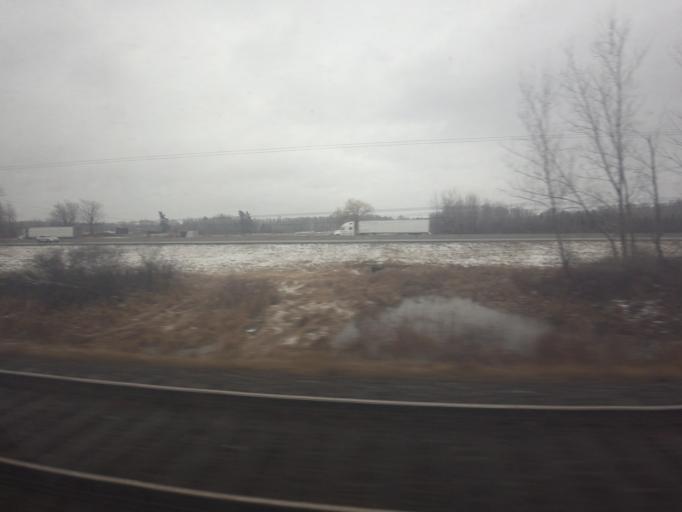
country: CA
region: Ontario
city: Kingston
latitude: 44.3179
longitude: -76.3730
